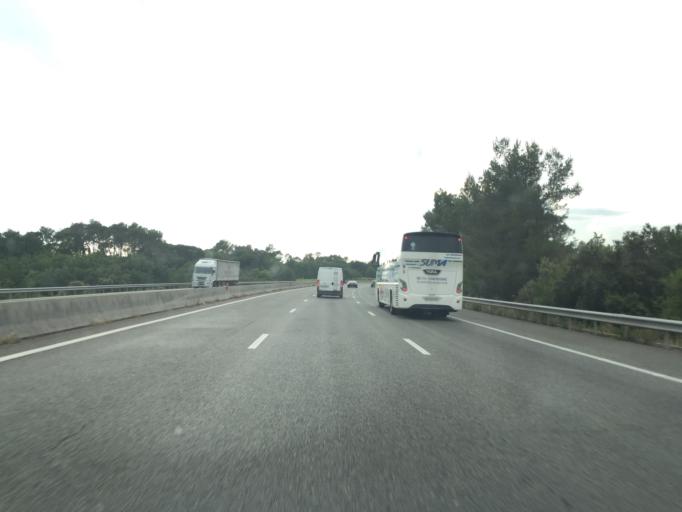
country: FR
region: Provence-Alpes-Cote d'Azur
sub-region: Departement du Var
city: Tourves
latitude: 43.4295
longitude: 5.9418
